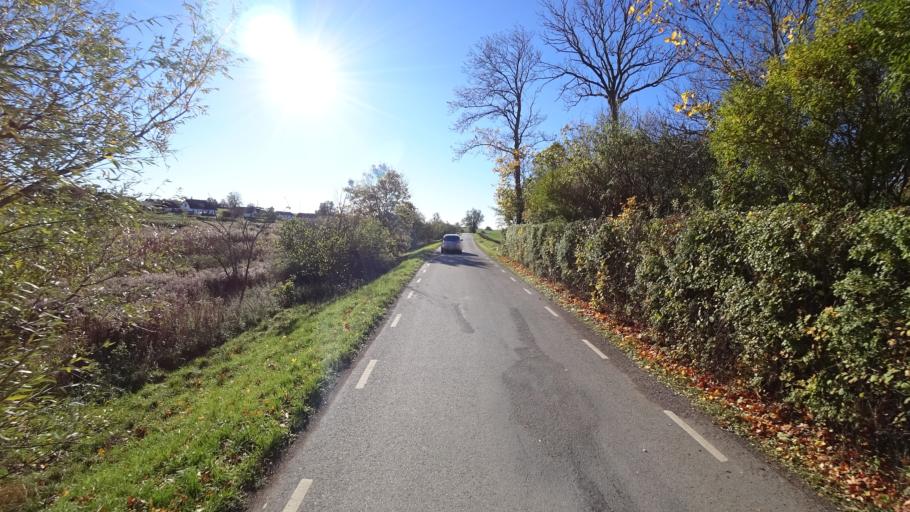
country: SE
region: Skane
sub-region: Lunds Kommun
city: Genarp
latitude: 55.6272
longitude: 13.3312
